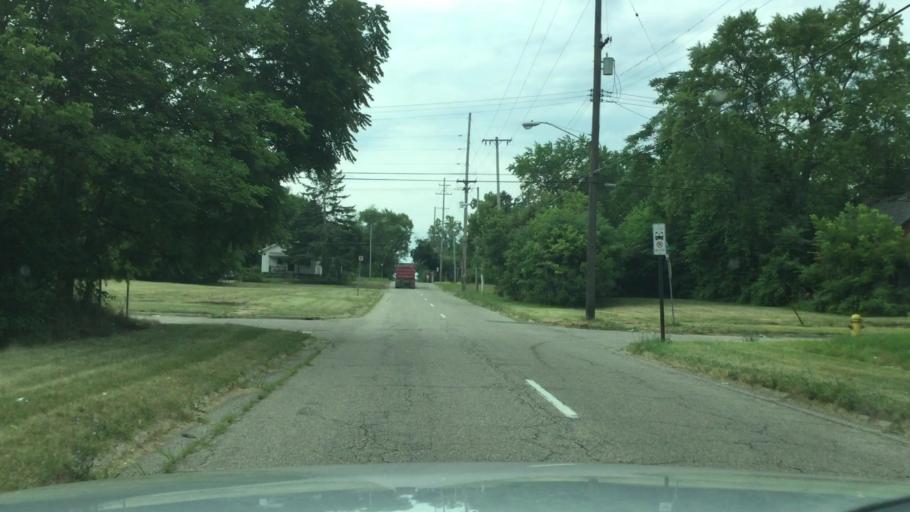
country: US
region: Michigan
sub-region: Genesee County
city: Beecher
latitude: 43.0600
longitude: -83.6845
